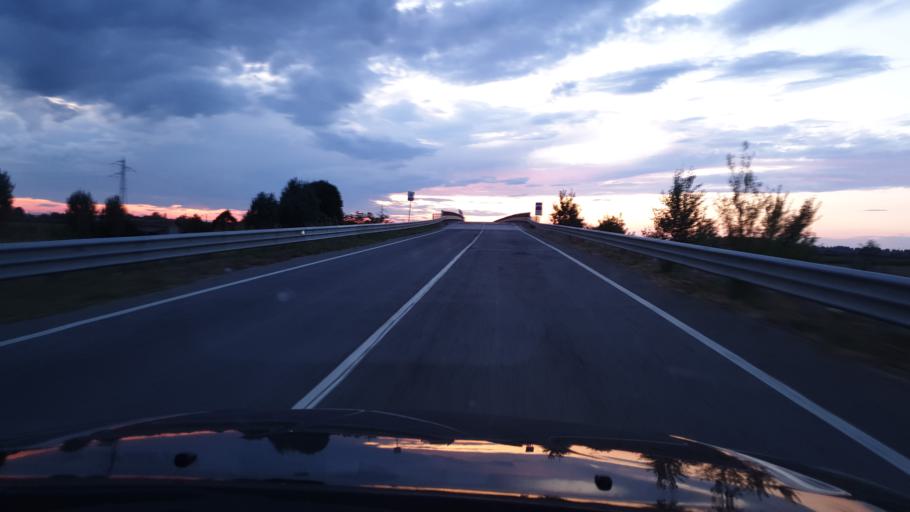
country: IT
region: Emilia-Romagna
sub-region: Provincia di Ravenna
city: Alfonsine
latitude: 44.5391
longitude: 12.0171
